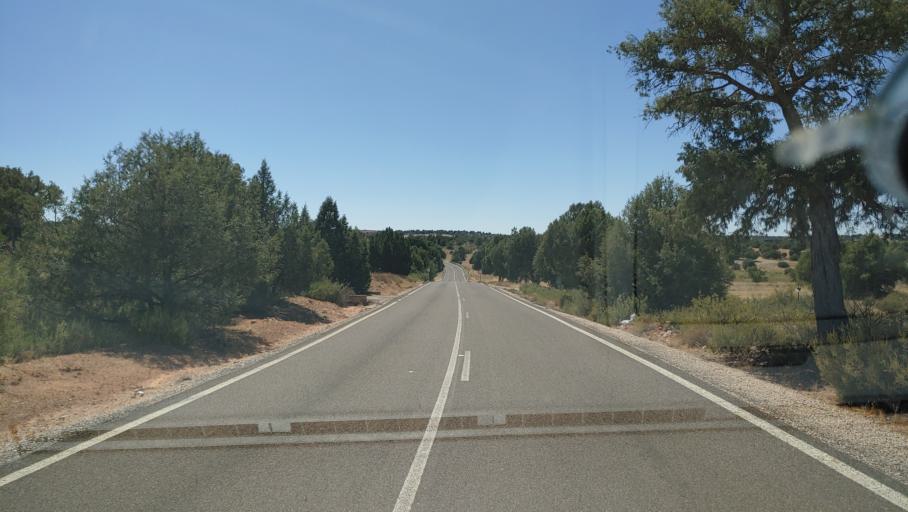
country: ES
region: Castille-La Mancha
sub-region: Provincia de Albacete
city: Ossa de Montiel
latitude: 38.8666
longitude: -2.7978
